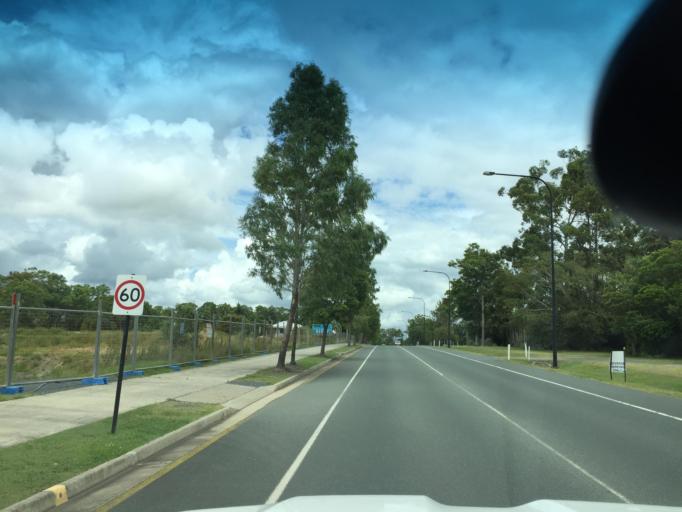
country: AU
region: Queensland
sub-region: Moreton Bay
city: Morayfield
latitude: -27.1257
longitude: 152.9922
